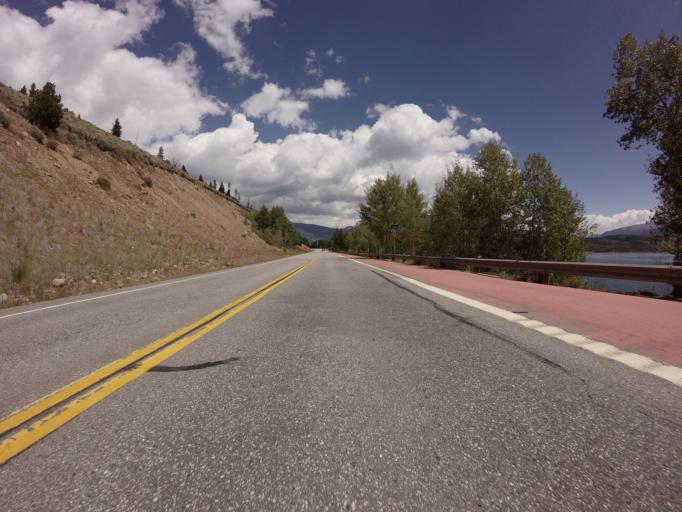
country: US
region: Colorado
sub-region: Summit County
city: Silverthorne
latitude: 39.6102
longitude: -106.0683
